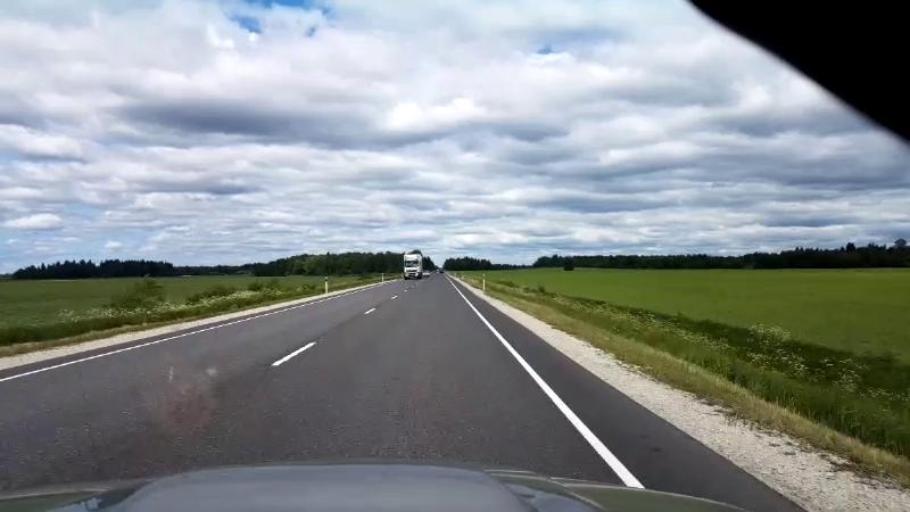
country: EE
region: Raplamaa
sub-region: Maerjamaa vald
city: Marjamaa
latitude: 58.8473
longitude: 24.4282
